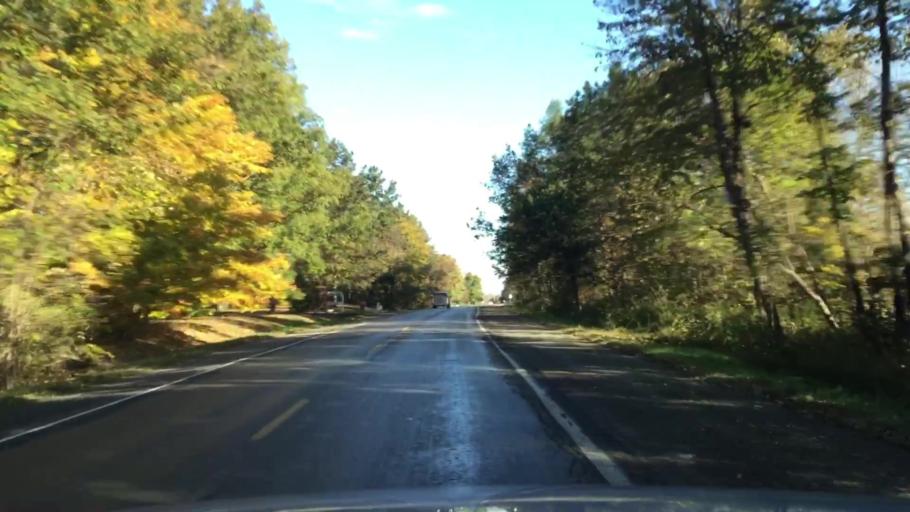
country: US
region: Michigan
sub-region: Shiawassee County
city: Durand
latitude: 42.9543
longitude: -83.9297
